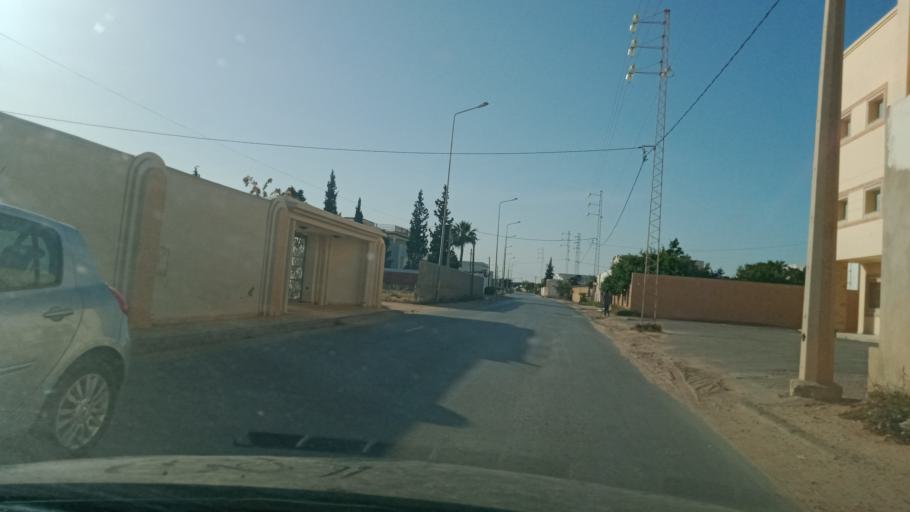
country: TN
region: Safaqis
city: Al Qarmadah
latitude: 34.8176
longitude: 10.7439
